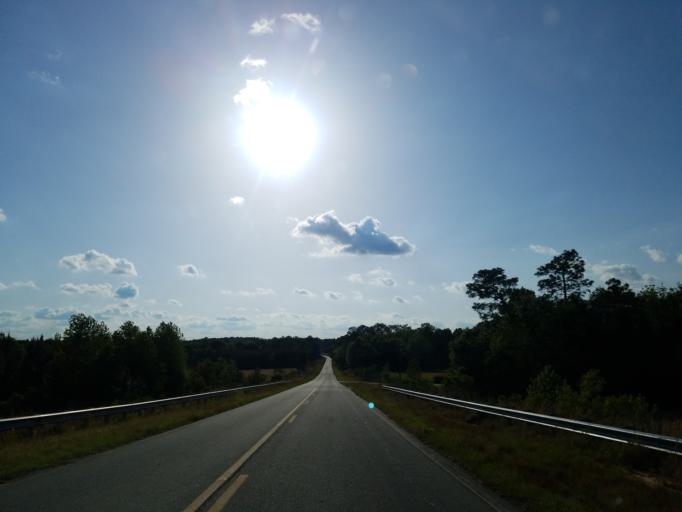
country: US
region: Georgia
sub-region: Turner County
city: Ashburn
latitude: 31.6088
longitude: -83.5666
